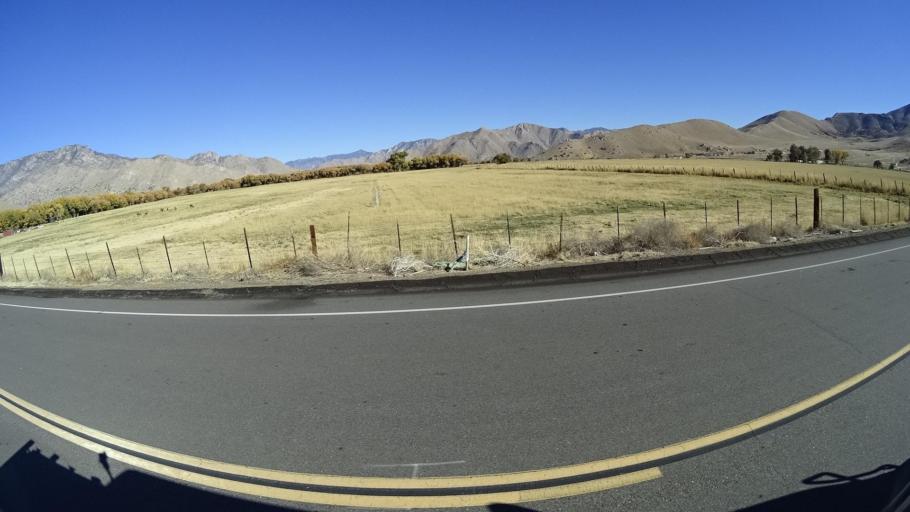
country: US
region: California
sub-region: Kern County
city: Weldon
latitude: 35.6655
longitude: -118.3226
